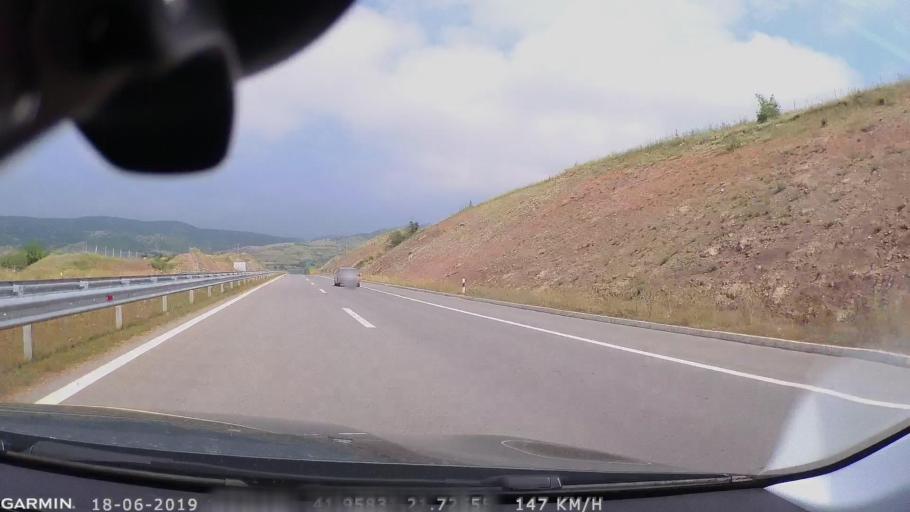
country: MK
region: Sveti Nikole
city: Gorobinci
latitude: 41.9317
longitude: 21.8271
